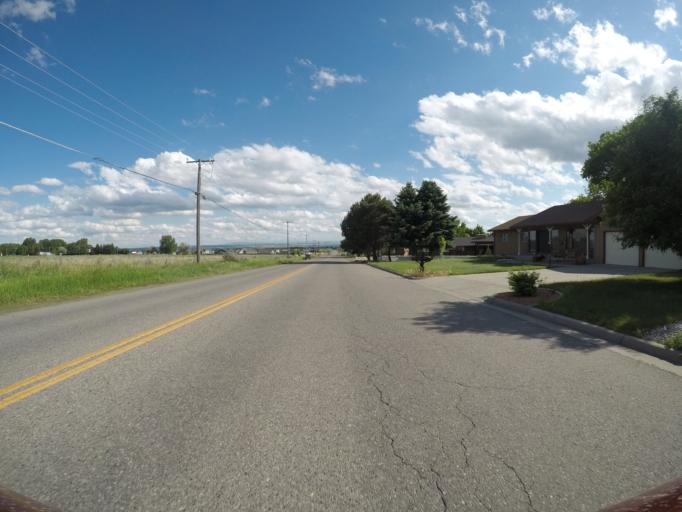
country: US
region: Montana
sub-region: Yellowstone County
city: Billings
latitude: 45.8009
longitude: -108.6527
